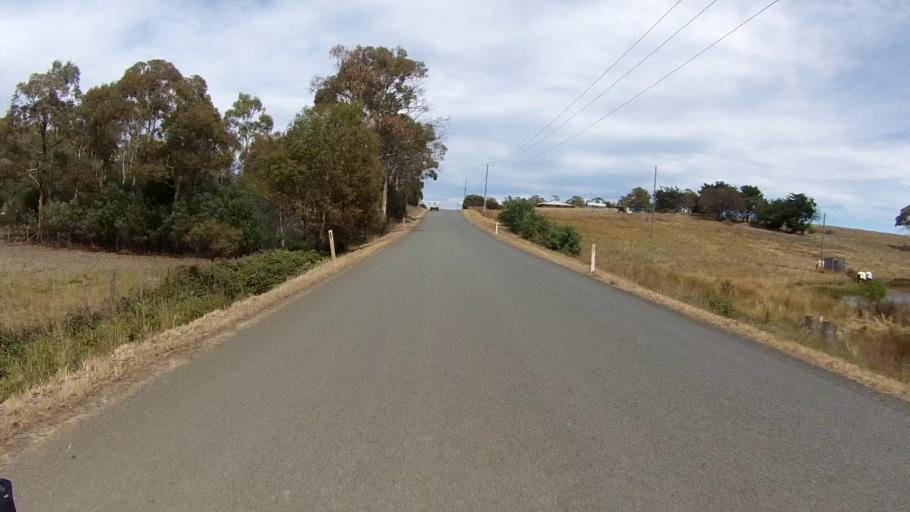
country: AU
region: Tasmania
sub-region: Sorell
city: Sorell
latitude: -42.8044
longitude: 147.6425
